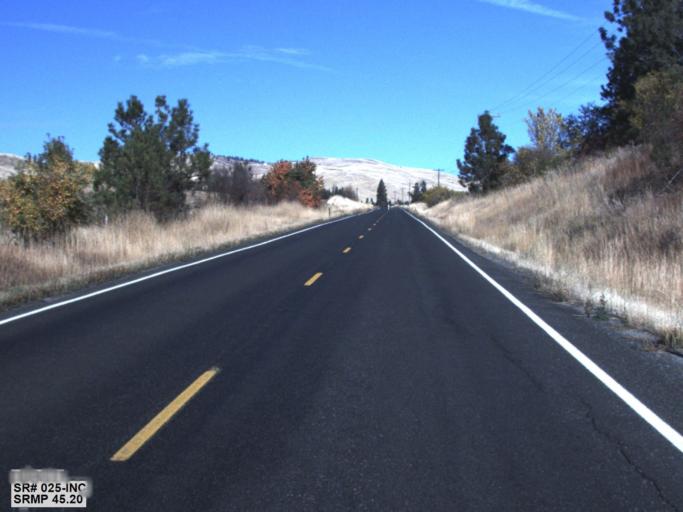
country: US
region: Washington
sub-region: Stevens County
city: Kettle Falls
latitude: 48.1476
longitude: -118.1779
